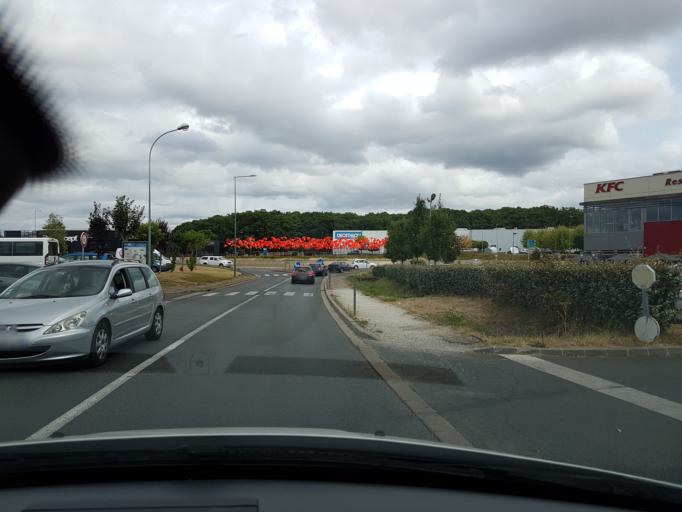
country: FR
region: Centre
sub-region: Departement d'Indre-et-Loire
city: Chambray-les-Tours
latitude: 47.3295
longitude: 0.7056
